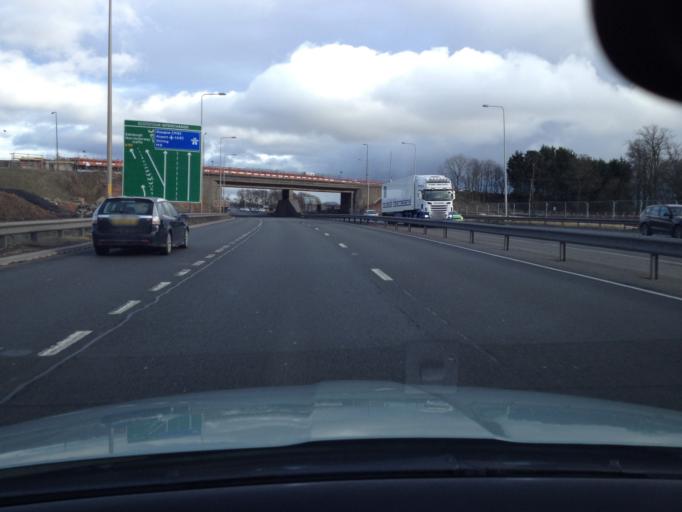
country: GB
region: Scotland
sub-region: Edinburgh
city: Queensferry
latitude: 55.9805
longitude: -3.3984
